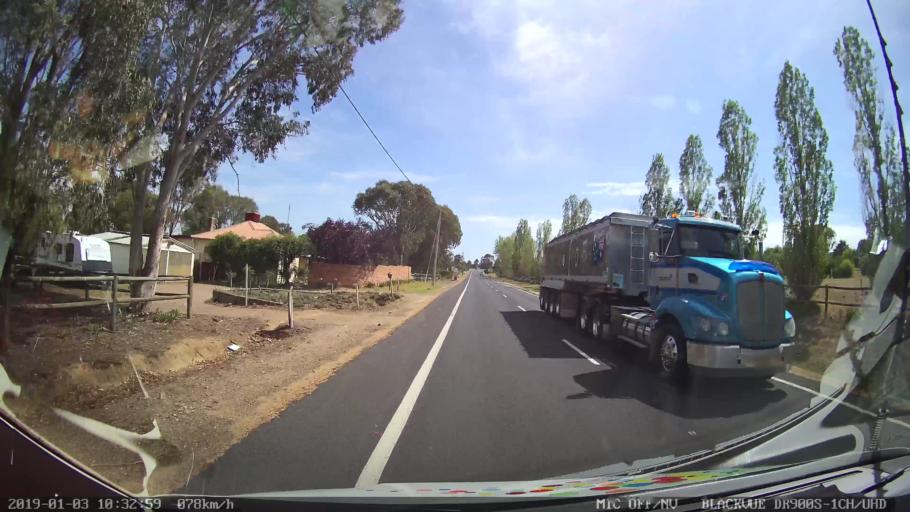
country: AU
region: New South Wales
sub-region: Young
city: Young
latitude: -34.3330
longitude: 148.2849
